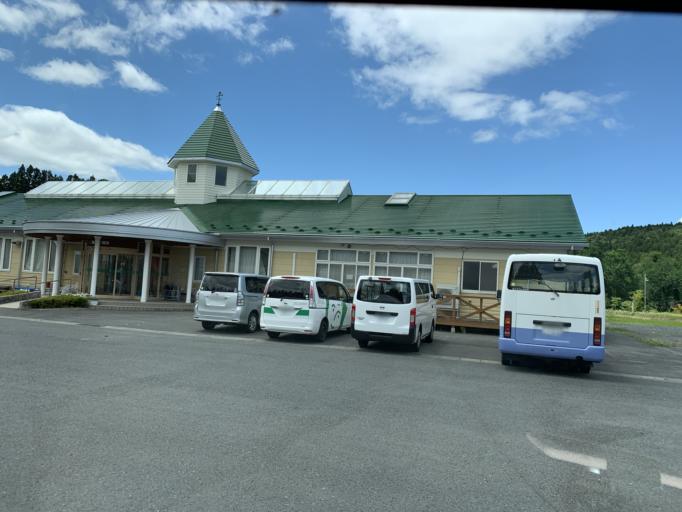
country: JP
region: Iwate
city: Ichinoseki
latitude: 38.9375
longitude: 141.0779
